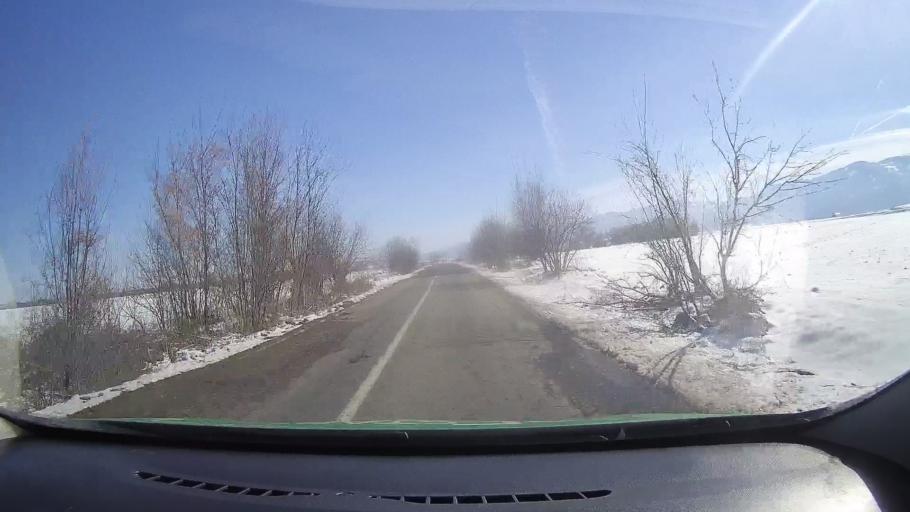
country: RO
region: Brasov
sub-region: Comuna Harseni
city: Harseni
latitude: 45.7290
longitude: 24.9809
